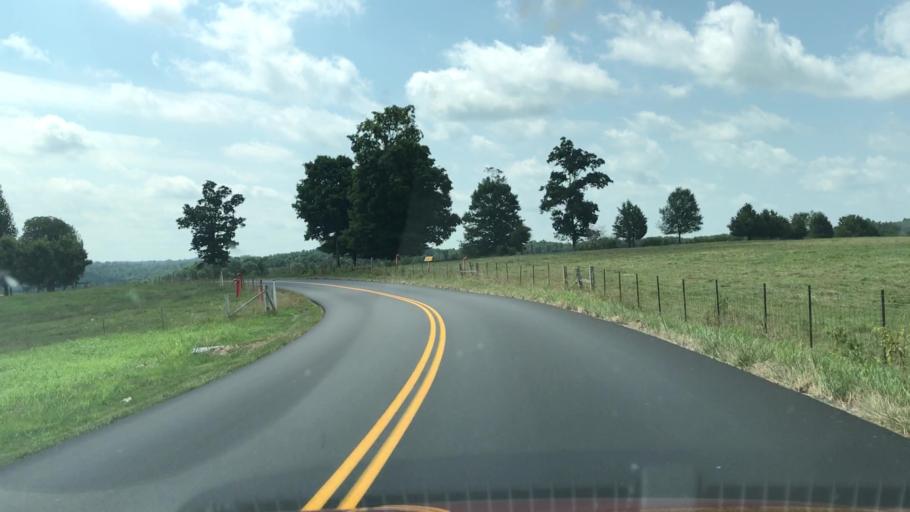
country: US
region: Kentucky
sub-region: Monroe County
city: Tompkinsville
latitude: 36.7427
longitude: -85.7601
